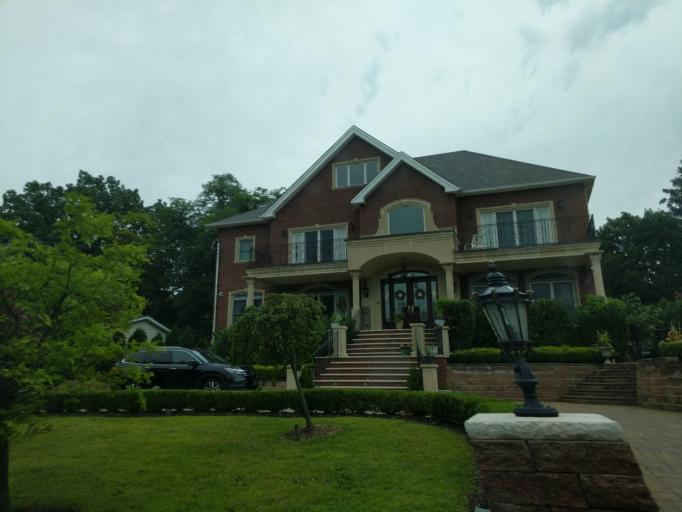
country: US
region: New York
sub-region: Richmond County
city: Staten Island
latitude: 40.5846
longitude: -74.1114
